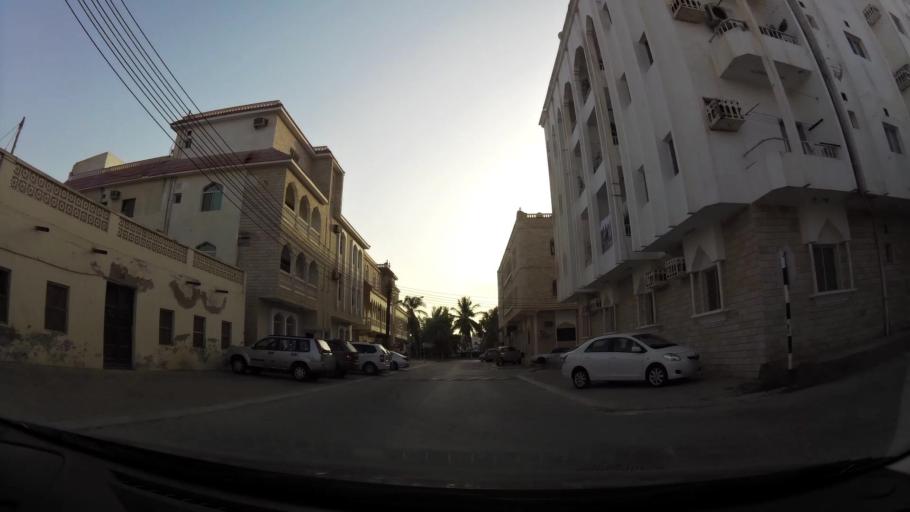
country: OM
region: Zufar
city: Salalah
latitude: 17.0136
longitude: 54.1073
